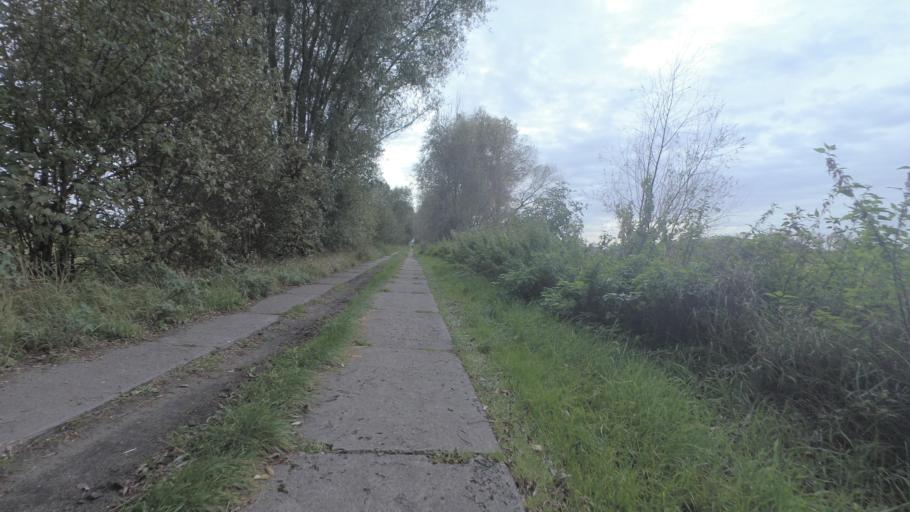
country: DE
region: Brandenburg
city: Grossbeeren
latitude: 52.2912
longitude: 13.3303
